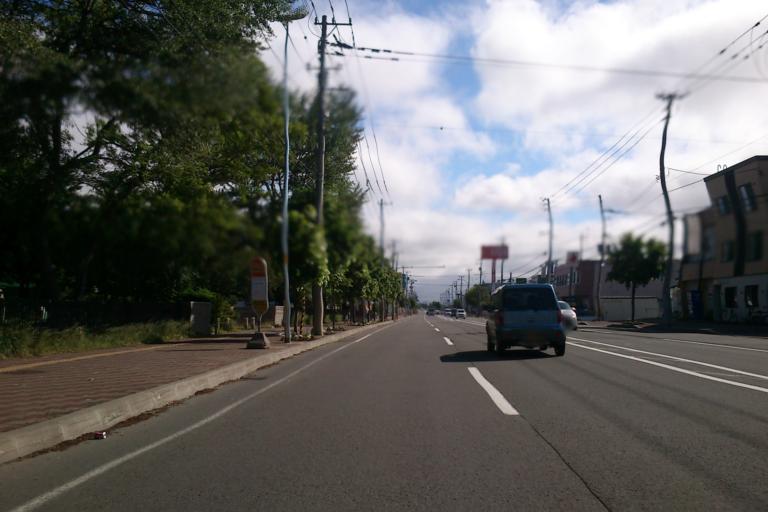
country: JP
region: Hokkaido
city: Sapporo
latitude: 43.1287
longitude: 141.2575
